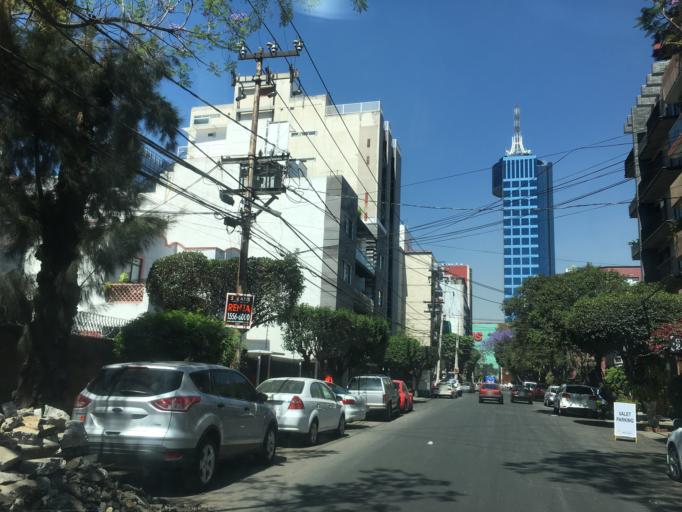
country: MX
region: Mexico City
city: Colonia del Valle
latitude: 19.3935
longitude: -99.1699
